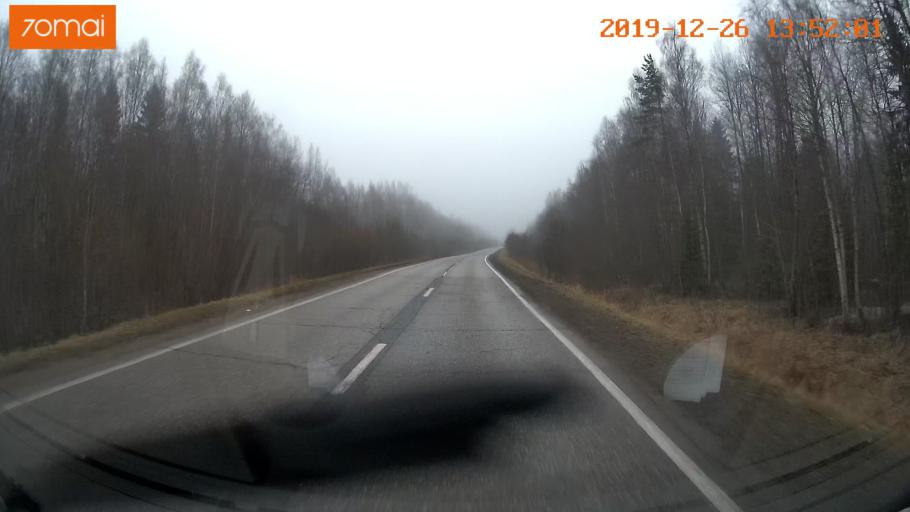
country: RU
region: Jaroslavl
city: Poshekhon'ye
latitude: 58.6370
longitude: 38.5978
